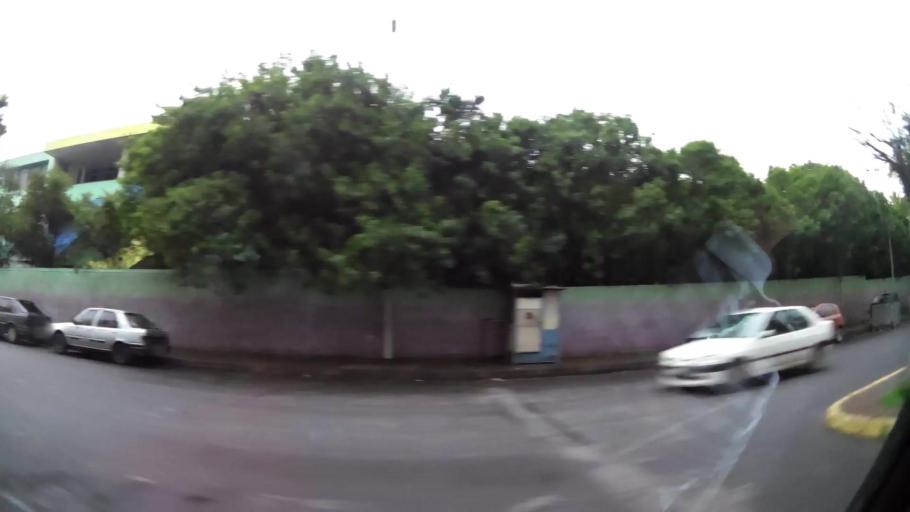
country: MA
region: Grand Casablanca
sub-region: Casablanca
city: Casablanca
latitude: 33.5551
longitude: -7.5900
